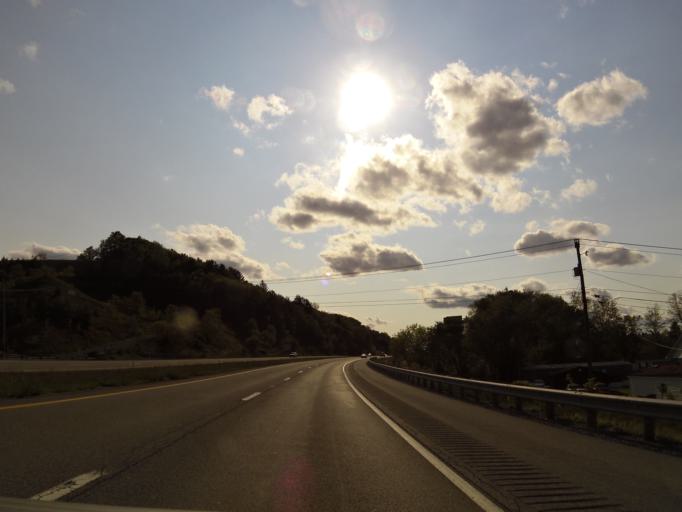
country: US
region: West Virginia
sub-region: Mercer County
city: Princeton
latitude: 37.3614
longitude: -81.0605
